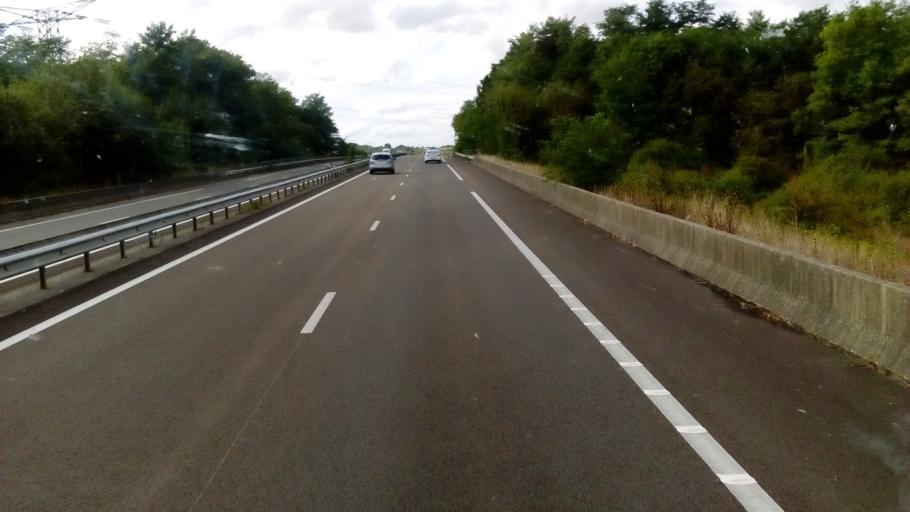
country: FR
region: Bourgogne
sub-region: Departement de la Nievre
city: Coulanges-les-Nevers
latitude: 47.0266
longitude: 3.1694
